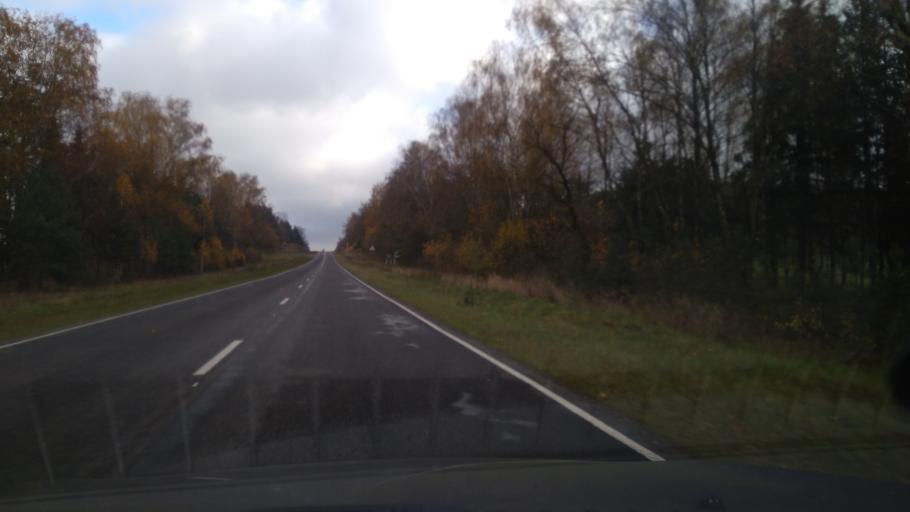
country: BY
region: Minsk
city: Urechcha
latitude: 53.2102
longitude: 27.9950
